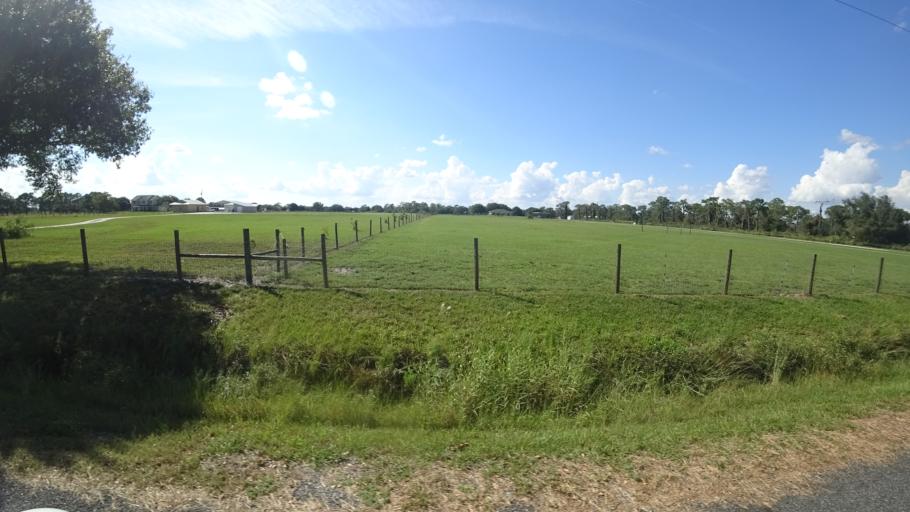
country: US
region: Florida
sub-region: Sarasota County
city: The Meadows
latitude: 27.4434
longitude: -82.2870
